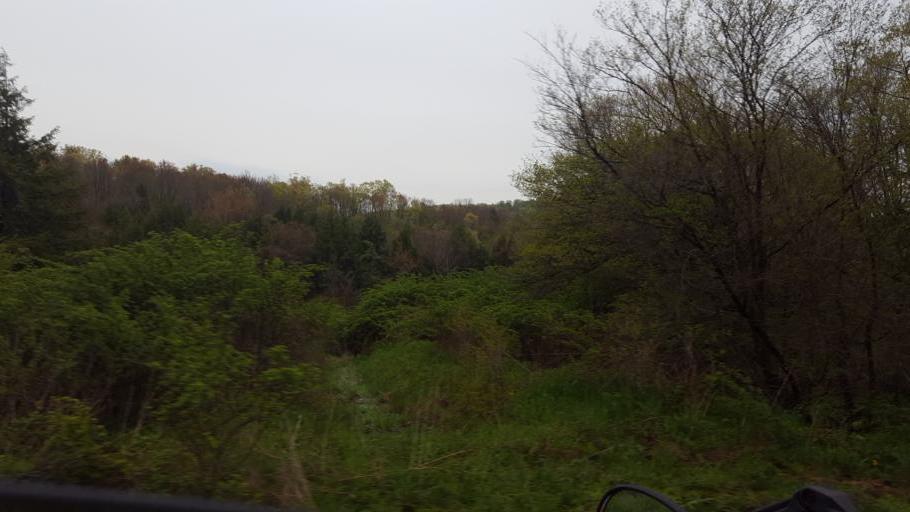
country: US
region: New York
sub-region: Allegany County
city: Andover
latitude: 41.9285
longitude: -77.7812
